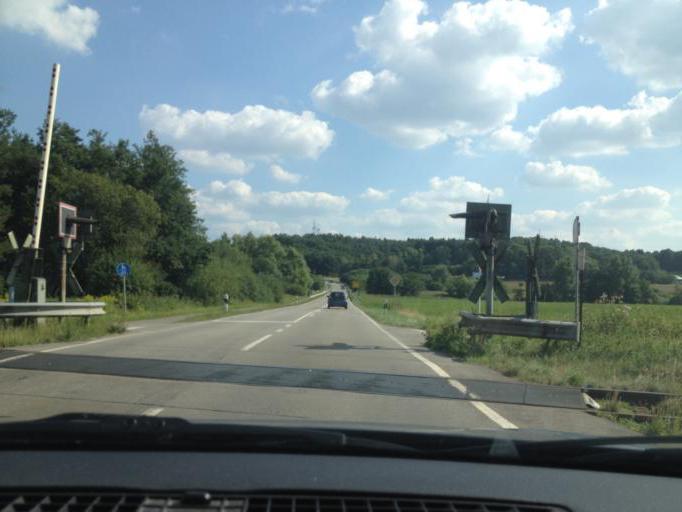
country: DE
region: Rheinland-Pfalz
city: Steinwenden
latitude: 49.4551
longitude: 7.5352
